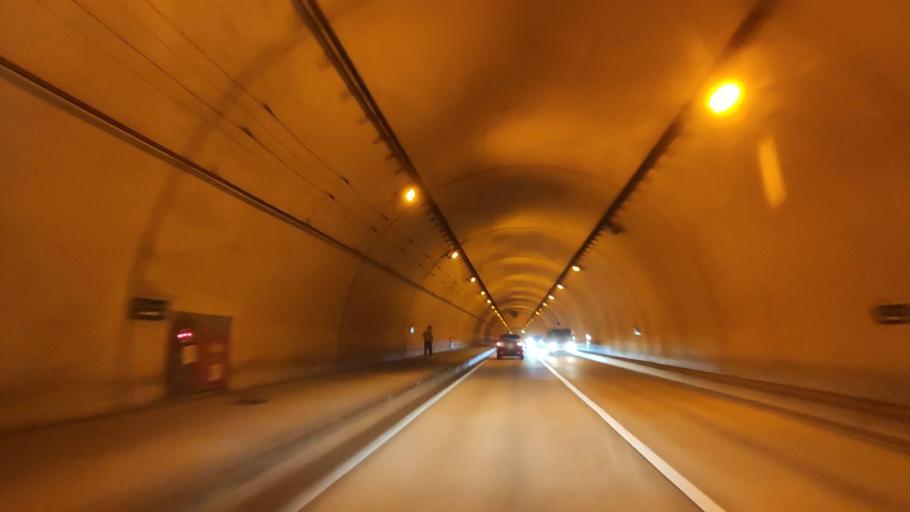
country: JP
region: Ehime
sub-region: Shikoku-chuo Shi
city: Matsuyama
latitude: 33.8780
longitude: 132.7131
